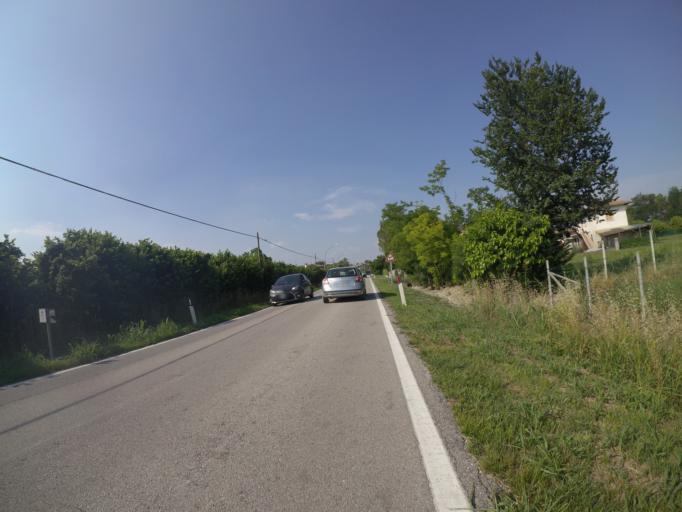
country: IT
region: Friuli Venezia Giulia
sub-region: Provincia di Udine
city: Camino al Tagliamento
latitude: 45.9410
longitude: 12.9627
